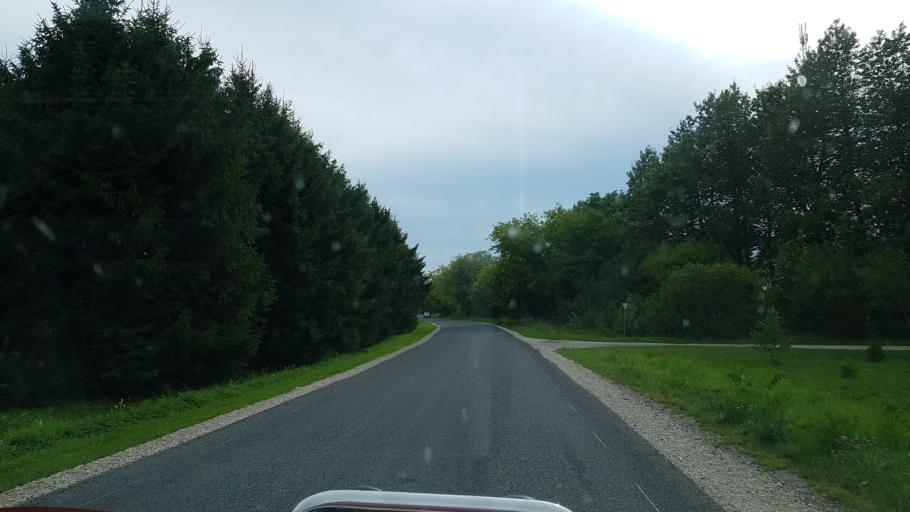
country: EE
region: Laeaene
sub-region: Lihula vald
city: Lihula
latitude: 58.8875
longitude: 23.8701
